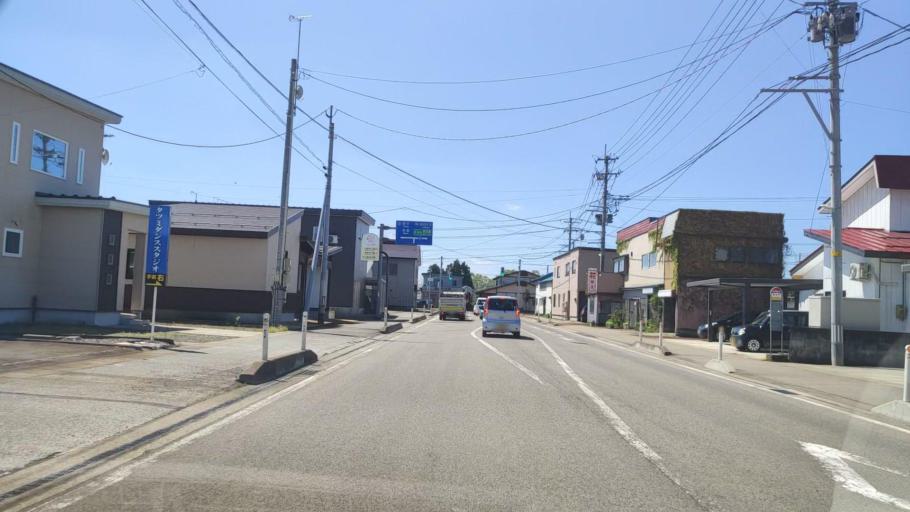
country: JP
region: Akita
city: Omagari
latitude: 39.4518
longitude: 140.4729
